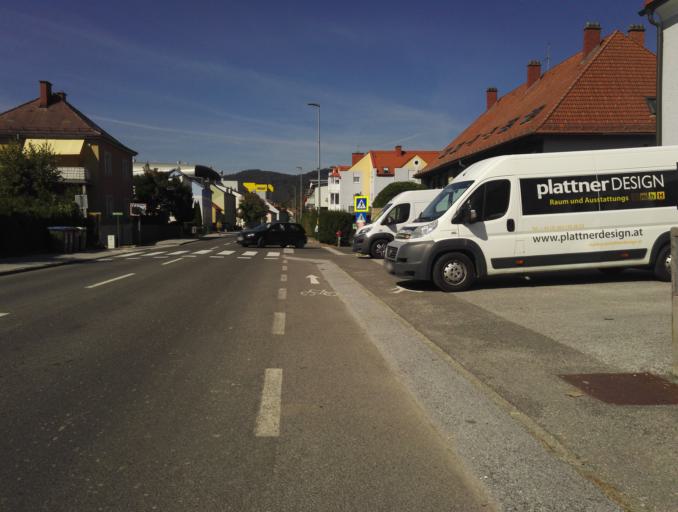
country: AT
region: Styria
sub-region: Politischer Bezirk Graz-Umgebung
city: Gratkorn
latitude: 47.1307
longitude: 15.3419
